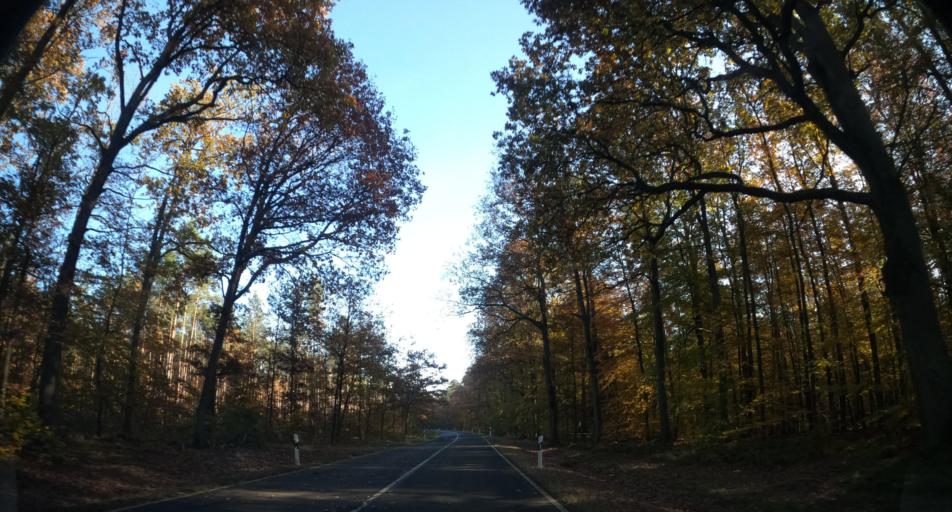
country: PL
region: West Pomeranian Voivodeship
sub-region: Powiat policki
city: Nowe Warpno
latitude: 53.6199
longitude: 14.2876
